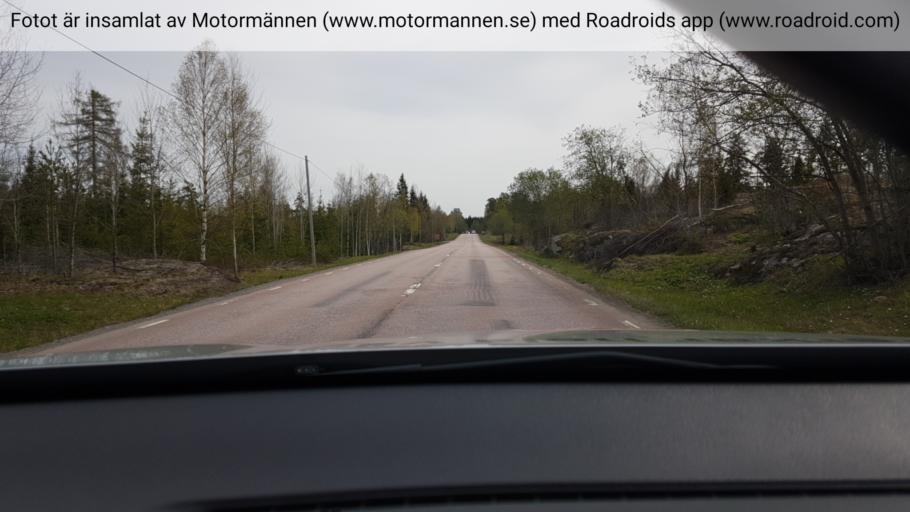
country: SE
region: Stockholm
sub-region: Norrtalje Kommun
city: Nykvarn
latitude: 59.8338
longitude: 18.0471
